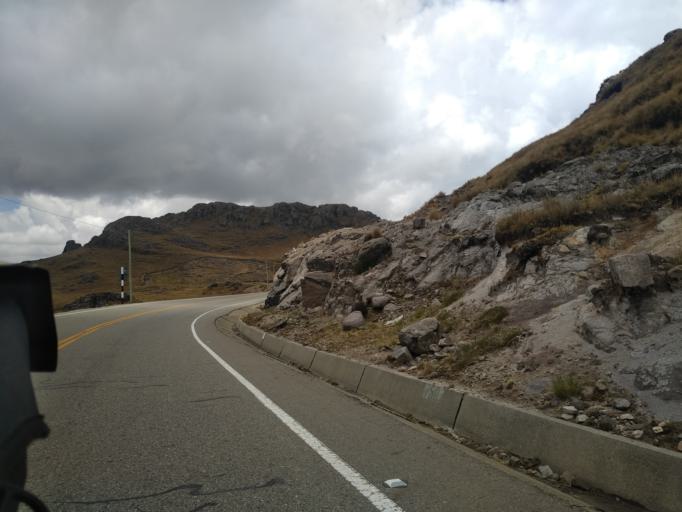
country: PE
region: La Libertad
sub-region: Provincia de Santiago de Chuco
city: Quiruvilca
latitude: -7.9731
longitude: -78.2082
